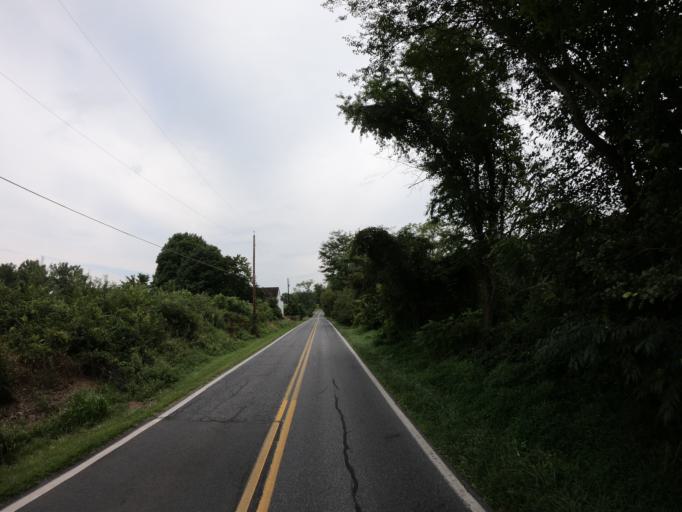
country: US
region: Maryland
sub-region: Montgomery County
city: Redland
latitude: 39.2144
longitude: -77.1257
